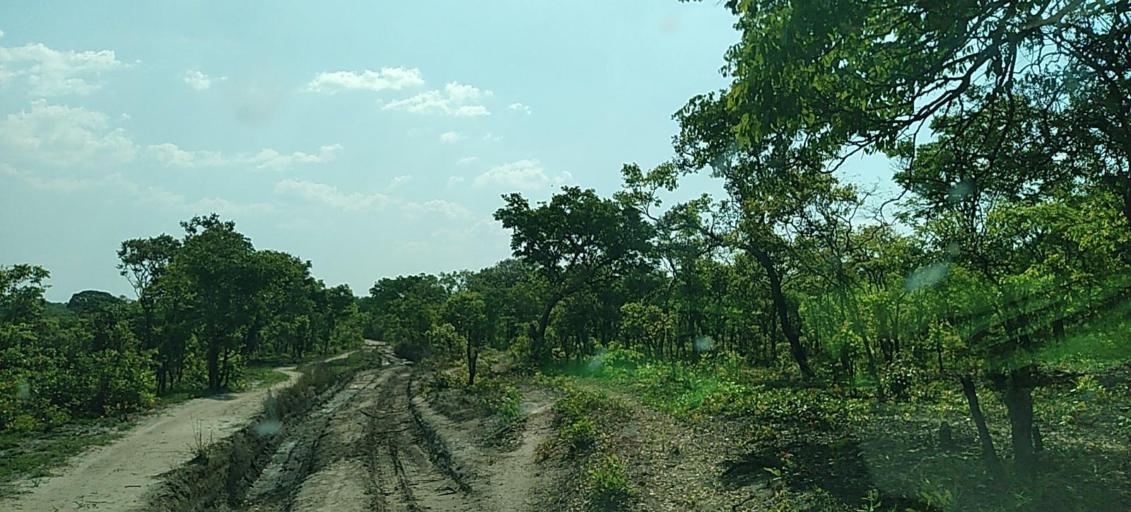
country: ZM
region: North-Western
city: Mwinilunga
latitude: -11.2768
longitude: 24.9304
